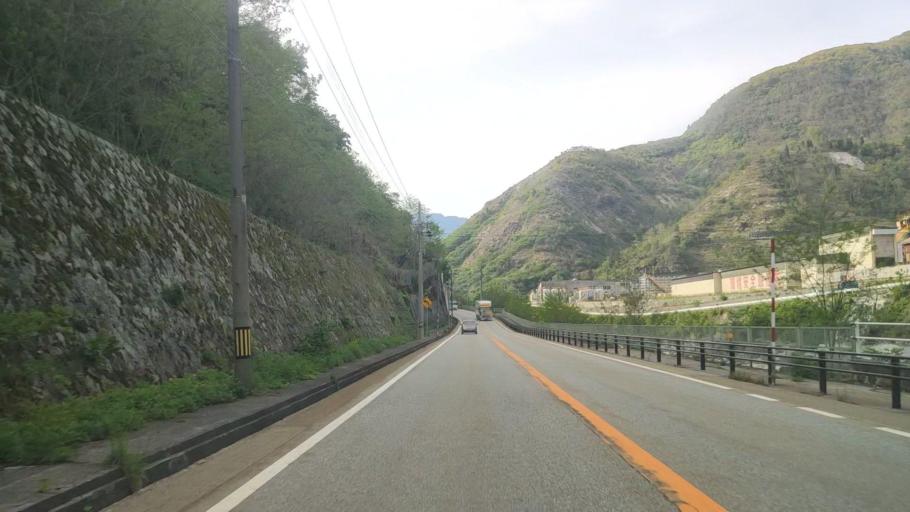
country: JP
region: Gifu
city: Takayama
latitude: 36.3459
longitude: 137.2945
